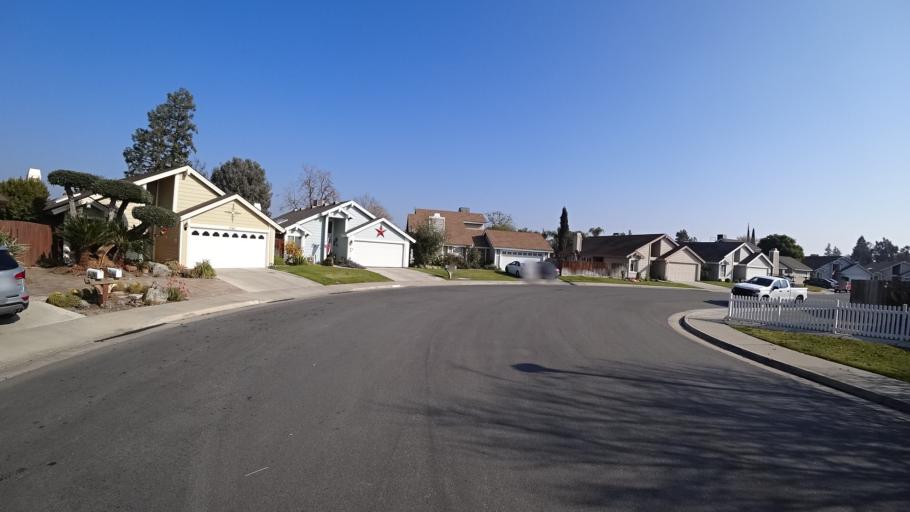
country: US
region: California
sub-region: Kern County
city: Greenacres
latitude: 35.3244
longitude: -119.0821
